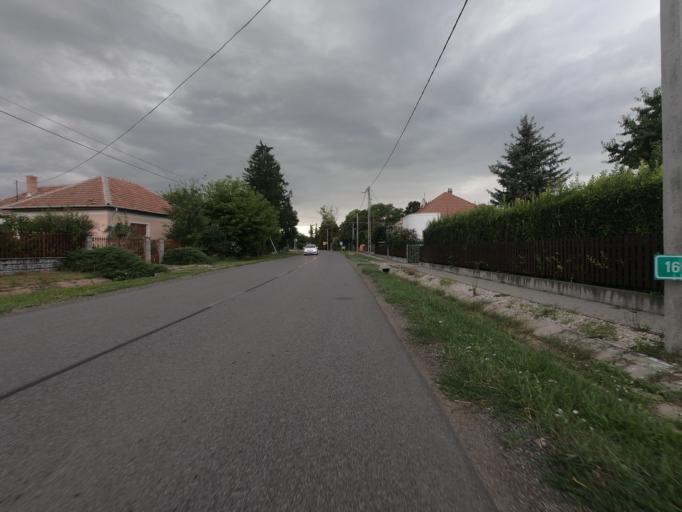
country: HU
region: Heves
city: Poroszlo
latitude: 47.6994
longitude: 20.6557
